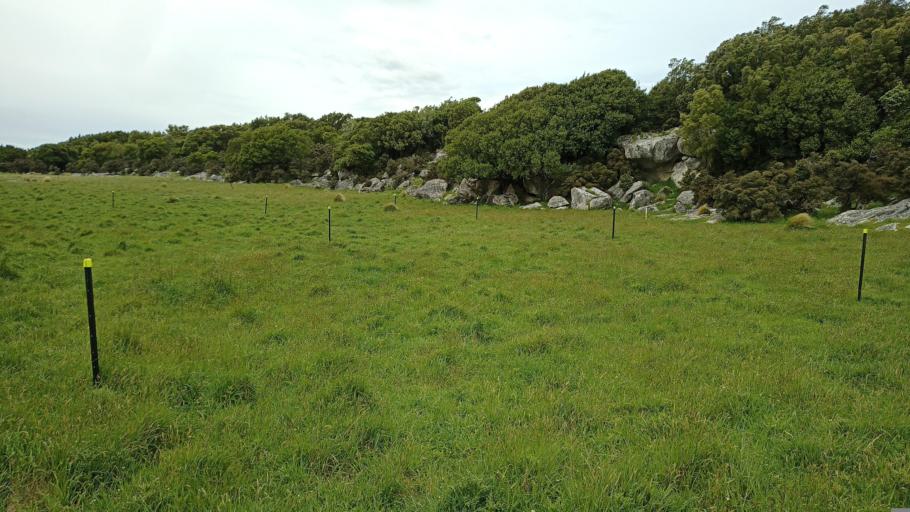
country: NZ
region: Canterbury
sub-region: Hurunui District
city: Amberley
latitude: -43.0734
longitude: 172.8467
